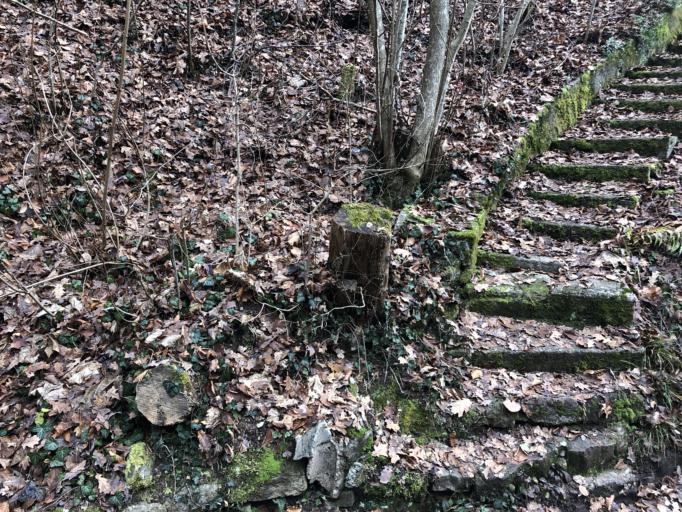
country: DE
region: Baden-Wuerttemberg
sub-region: Tuebingen Region
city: Tuebingen
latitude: 48.5087
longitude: 9.0265
